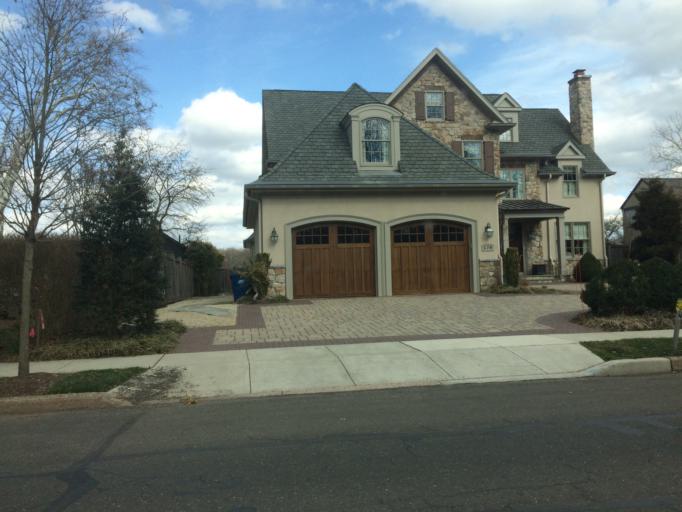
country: US
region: Pennsylvania
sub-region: Bucks County
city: New Hope
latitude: 40.3702
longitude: -74.9538
